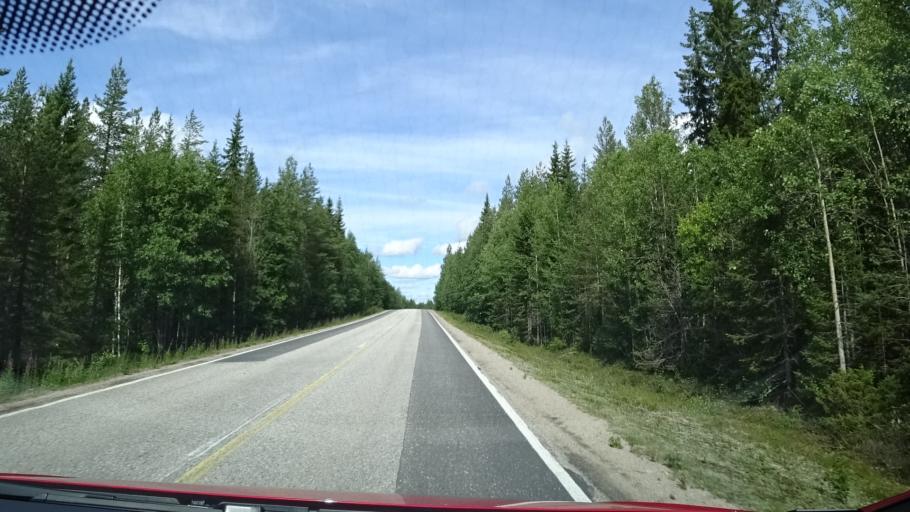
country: FI
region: Kainuu
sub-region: Kehys-Kainuu
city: Kuhmo
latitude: 64.4417
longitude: 29.8023
